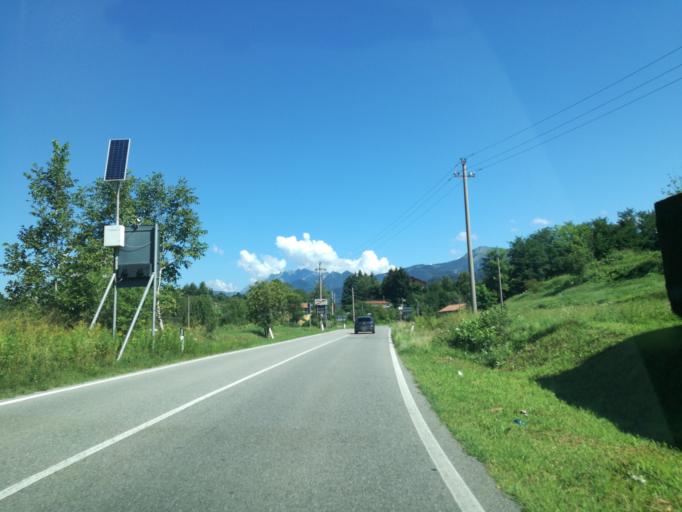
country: IT
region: Lombardy
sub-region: Provincia di Lecco
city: Arlate
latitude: 45.7300
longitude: 9.4410
